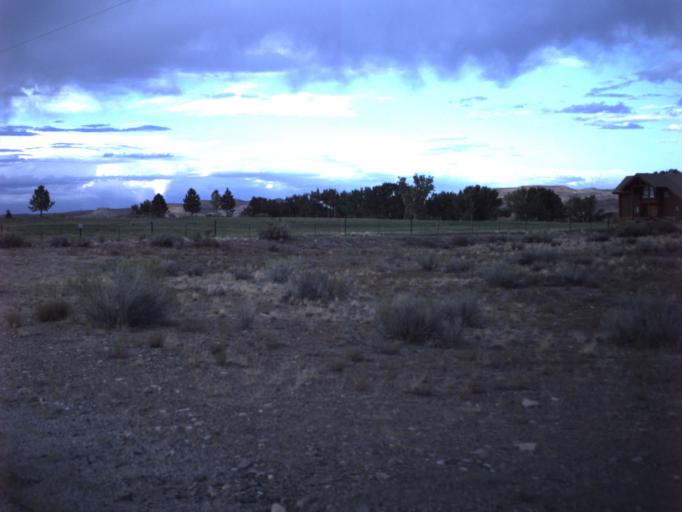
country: US
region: Utah
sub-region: Grand County
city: Moab
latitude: 38.8467
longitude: -109.2824
